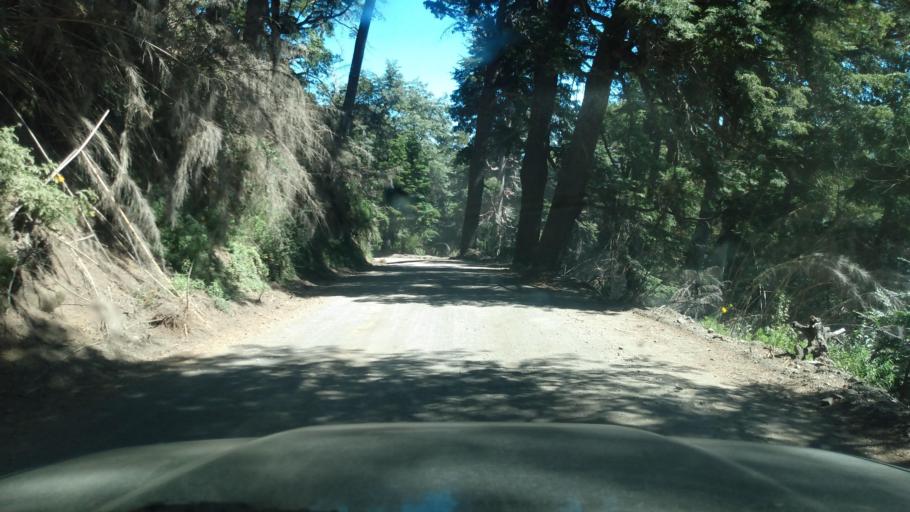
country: AR
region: Neuquen
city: Villa La Angostura
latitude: -40.6066
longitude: -71.6430
